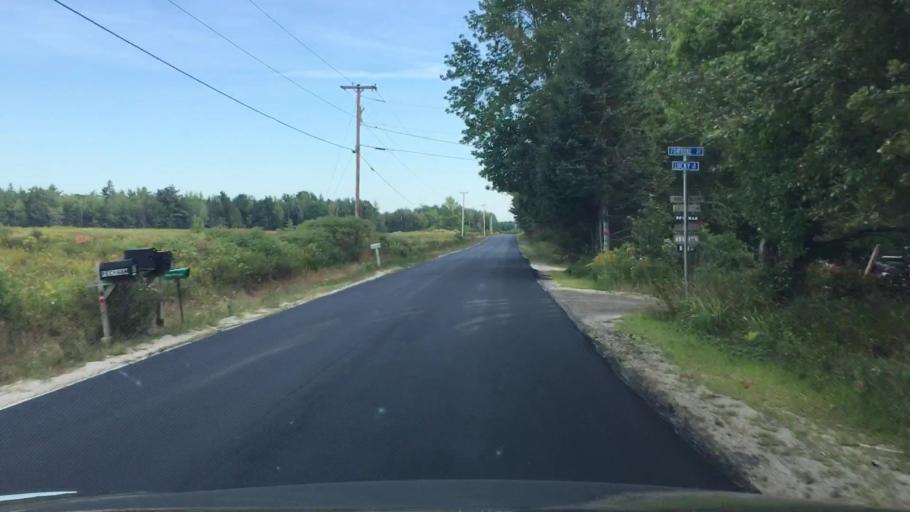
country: US
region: Maine
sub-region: Hancock County
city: Surry
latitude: 44.5355
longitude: -68.6143
